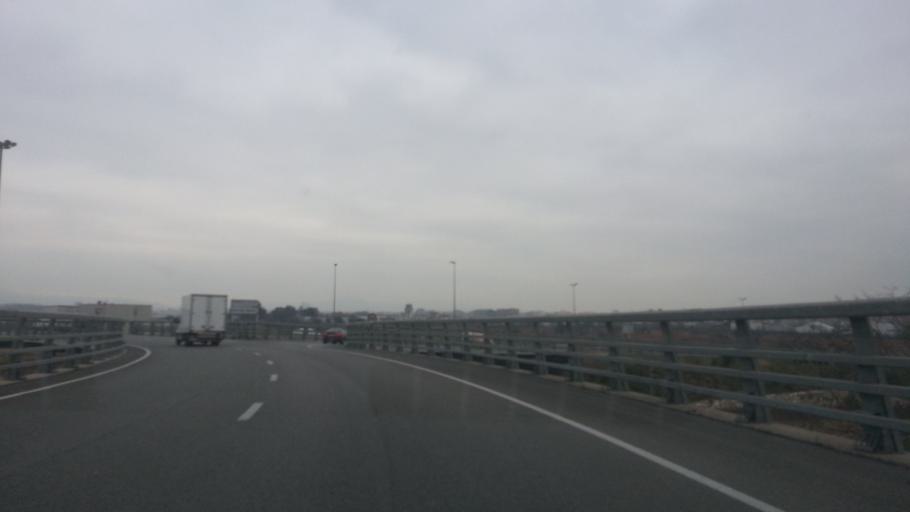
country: ES
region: Catalonia
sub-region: Provincia de Barcelona
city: Barbera del Valles
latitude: 41.5139
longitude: 2.1025
